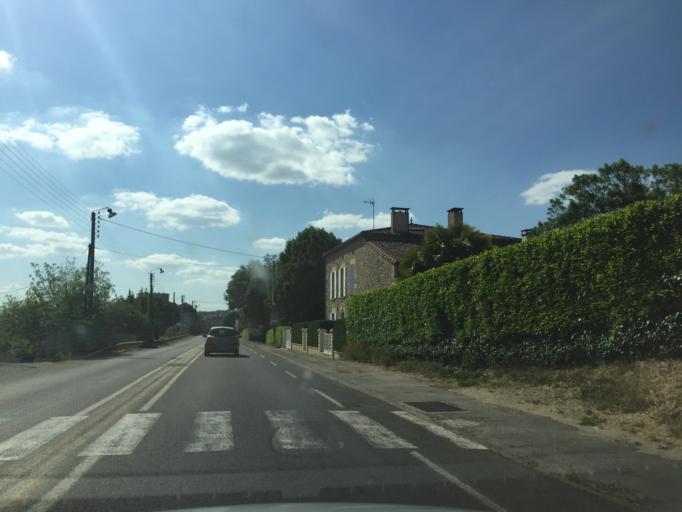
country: FR
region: Aquitaine
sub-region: Departement de la Gironde
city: La Reole
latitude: 44.5804
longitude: -0.0270
